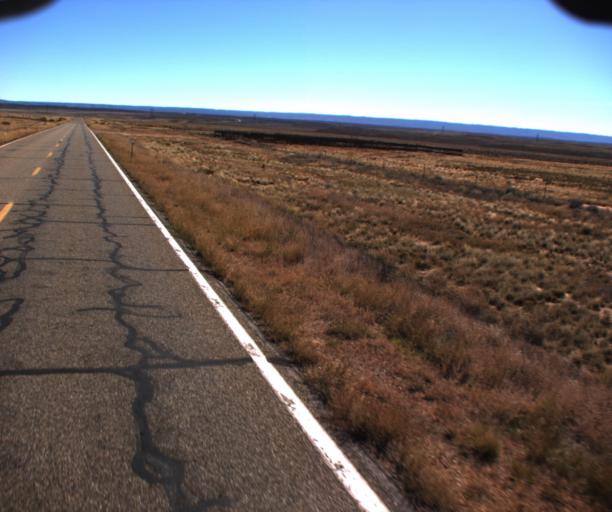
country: US
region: Arizona
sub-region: Coconino County
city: Fredonia
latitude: 36.9232
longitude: -112.4516
